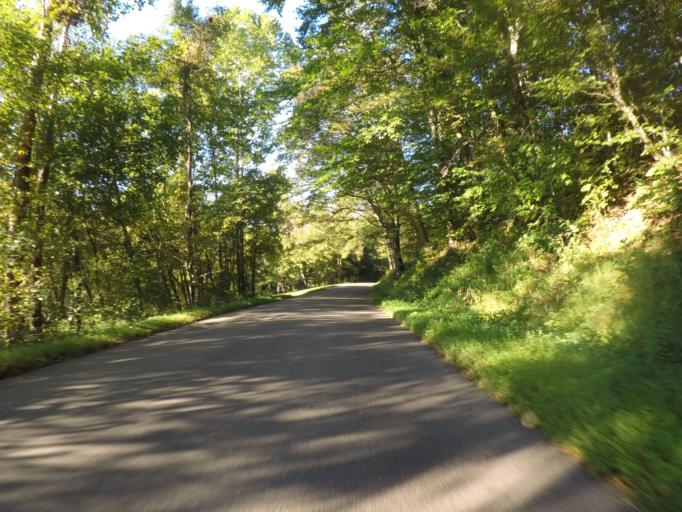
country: US
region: Ohio
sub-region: Lawrence County
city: Coal Grove
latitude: 38.5523
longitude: -82.5549
